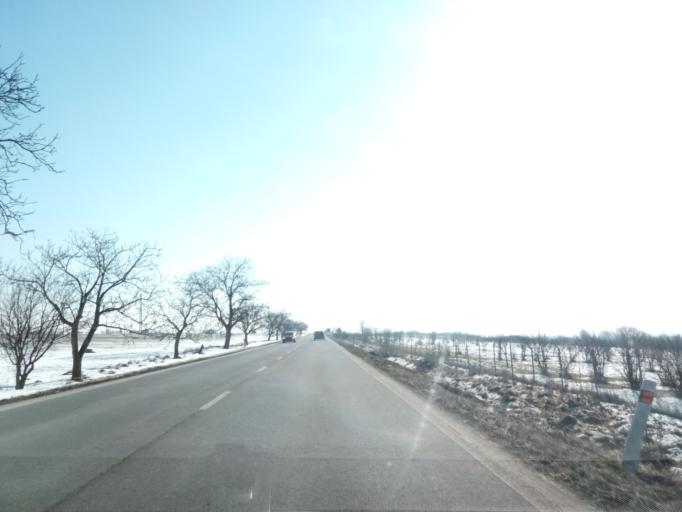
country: SK
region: Kosicky
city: Secovce
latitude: 48.7270
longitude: 21.6019
